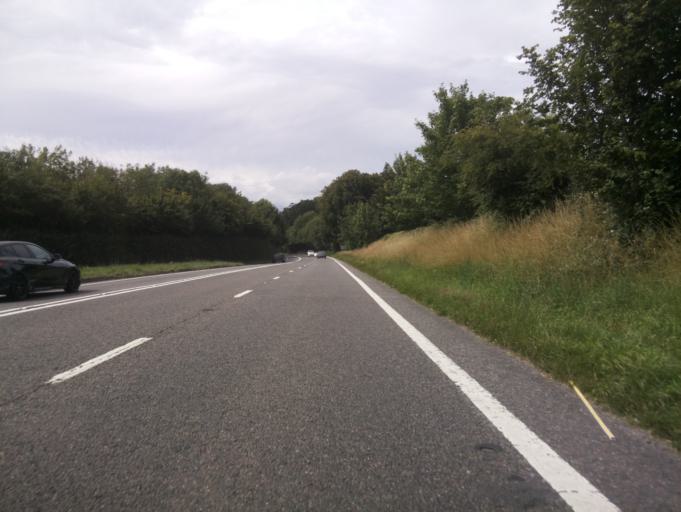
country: GB
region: England
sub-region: Somerset
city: Yeovil
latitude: 50.8544
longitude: -2.5860
